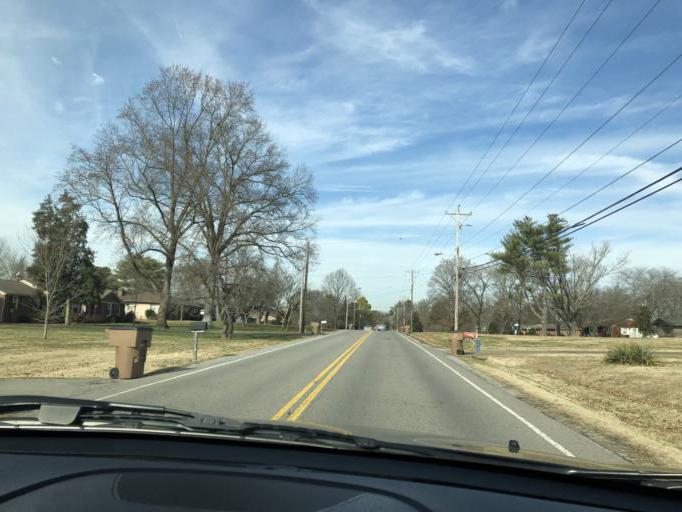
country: US
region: Tennessee
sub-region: Davidson County
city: Lakewood
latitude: 36.2034
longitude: -86.6783
